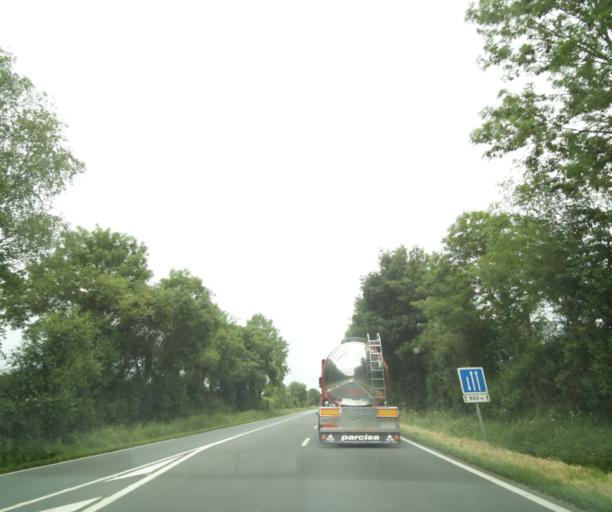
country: FR
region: Poitou-Charentes
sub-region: Departement des Deux-Sevres
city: Champdeniers-Saint-Denis
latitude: 46.4852
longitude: -0.3548
